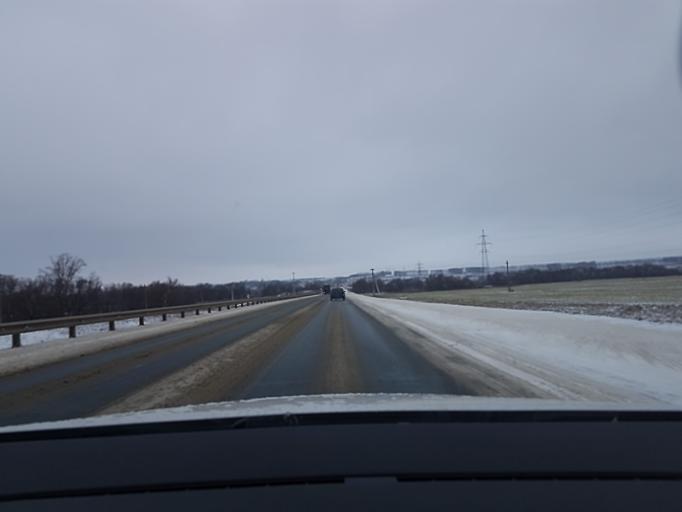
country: RU
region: Rjazan
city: Mikhaylov
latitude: 54.2093
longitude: 39.0832
